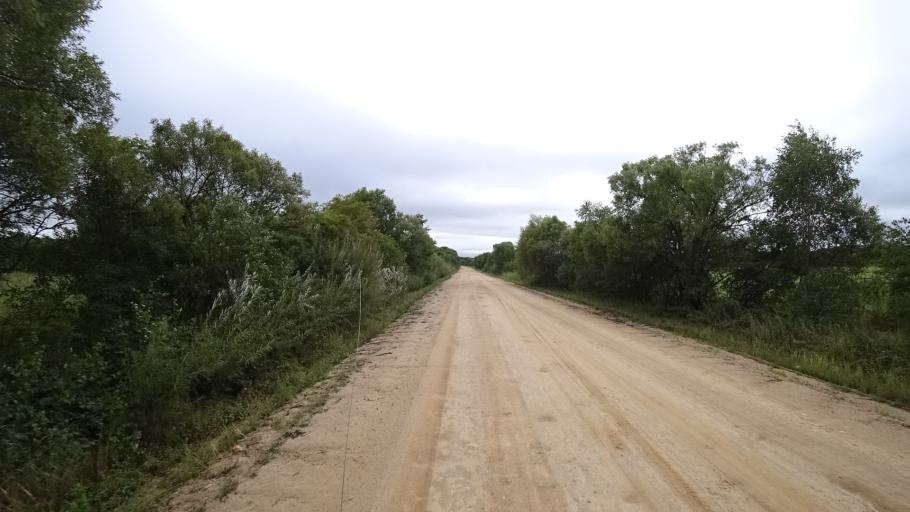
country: RU
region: Primorskiy
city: Monastyrishche
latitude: 44.1035
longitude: 132.6091
